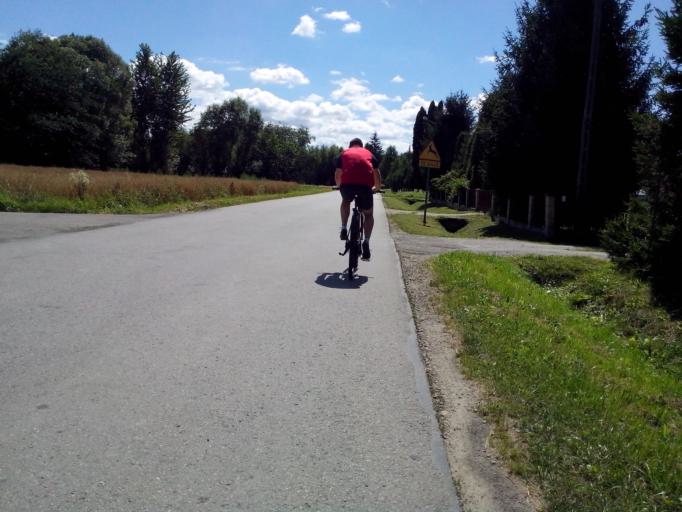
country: PL
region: Subcarpathian Voivodeship
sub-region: Powiat brzozowski
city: Blizne
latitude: 49.7816
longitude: 21.9918
